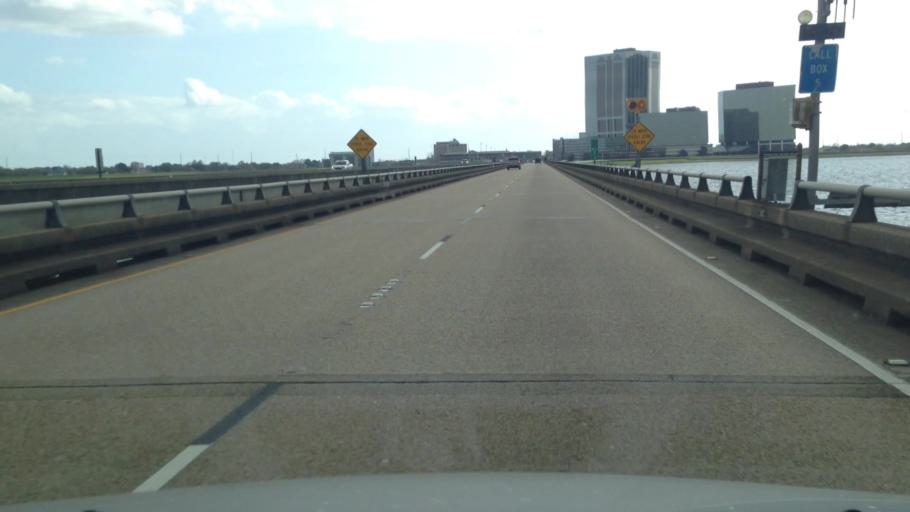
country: US
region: Louisiana
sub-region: Jefferson Parish
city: Metairie
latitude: 30.0280
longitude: -90.1530
